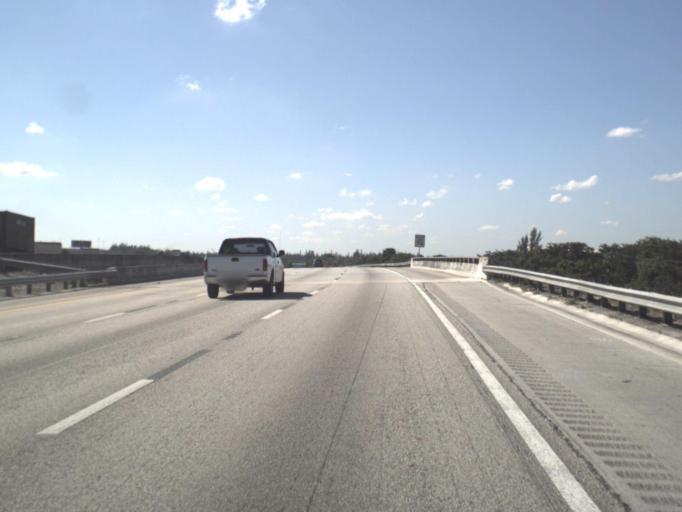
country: US
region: Florida
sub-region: Miami-Dade County
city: Palm Springs North
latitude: 25.8941
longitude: -80.3880
